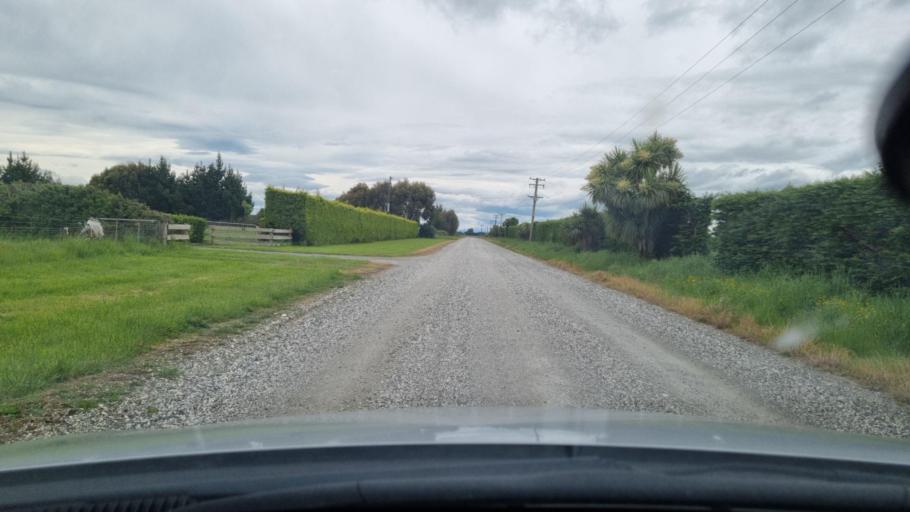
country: NZ
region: Southland
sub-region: Invercargill City
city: Invercargill
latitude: -46.3743
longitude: 168.2991
